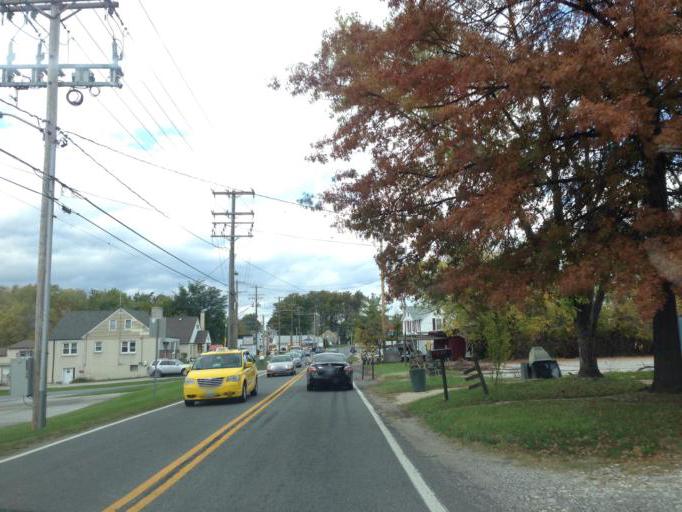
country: US
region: Maryland
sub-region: Baltimore County
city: Milford Mill
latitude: 39.3399
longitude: -76.7615
